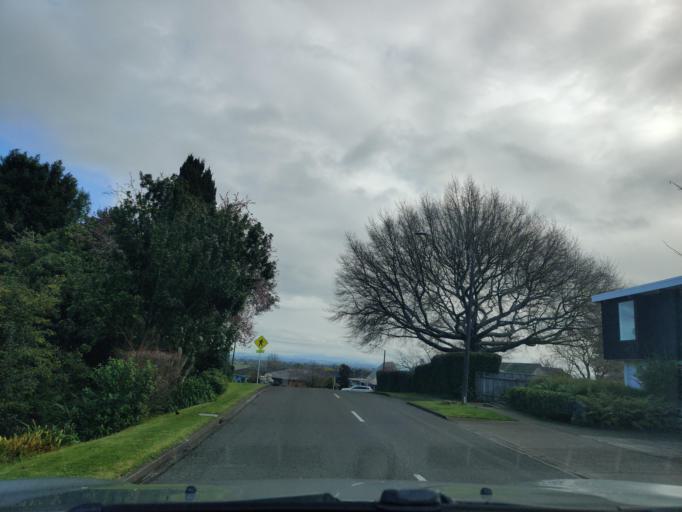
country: NZ
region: Hawke's Bay
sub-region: Hastings District
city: Hastings
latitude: -39.6721
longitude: 176.8861
